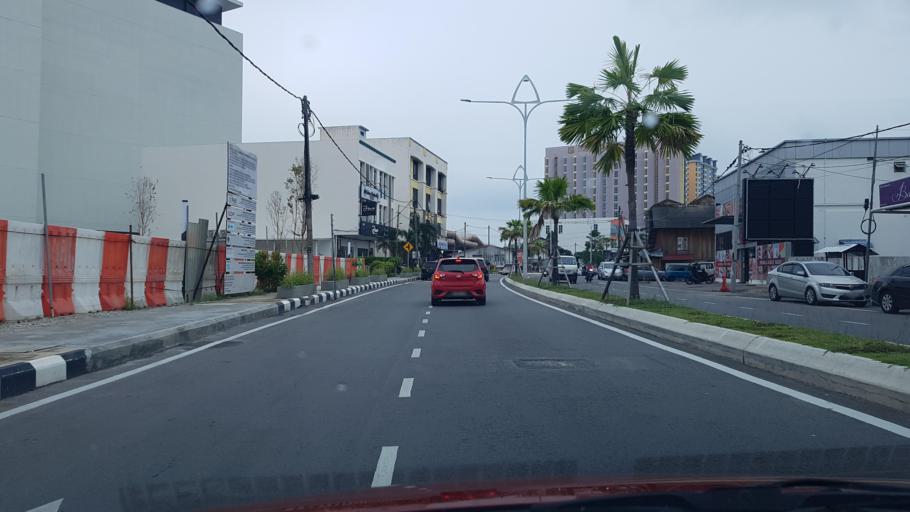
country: MY
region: Terengganu
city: Kuala Terengganu
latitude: 5.3362
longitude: 103.1442
